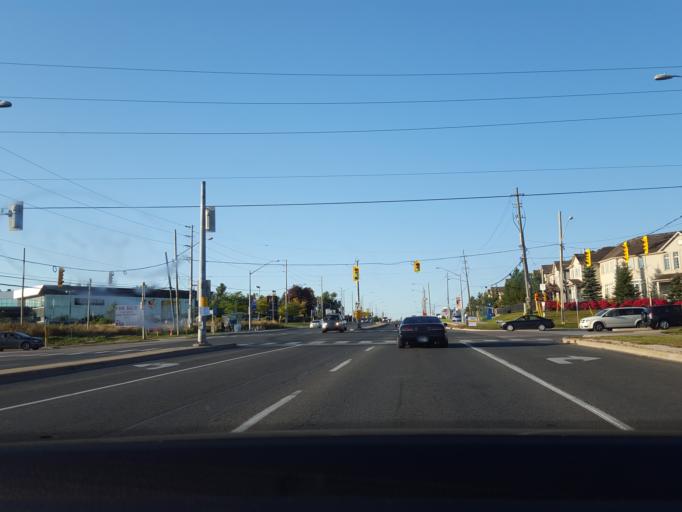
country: CA
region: Ontario
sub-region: York
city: Richmond Hill
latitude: 43.9074
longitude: -79.4456
